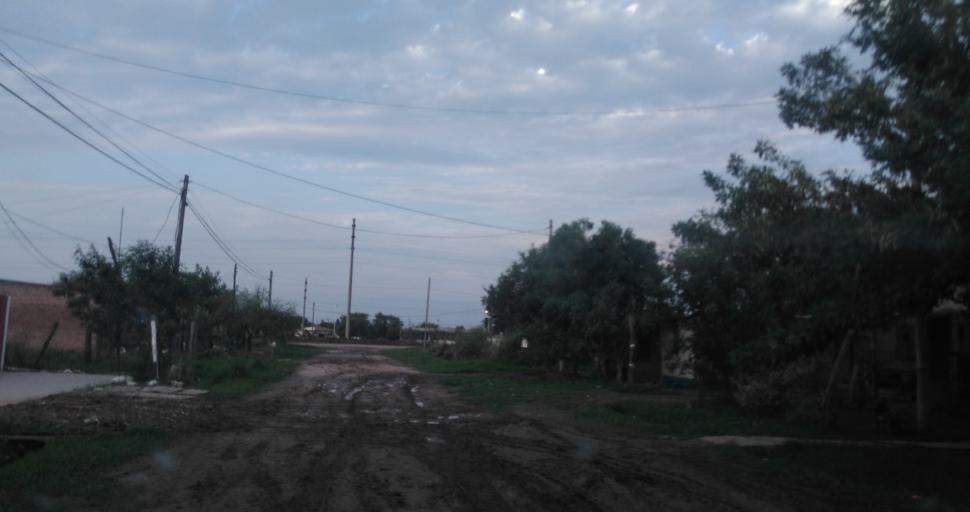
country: AR
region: Chaco
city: Resistencia
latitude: -27.4789
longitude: -59.0014
